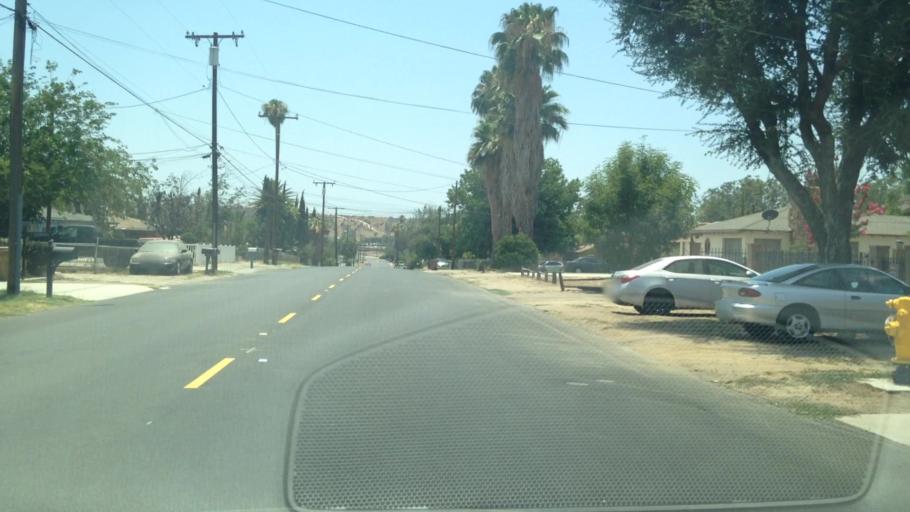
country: US
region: California
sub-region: Riverside County
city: Calimesa
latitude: 34.0251
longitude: -117.0955
